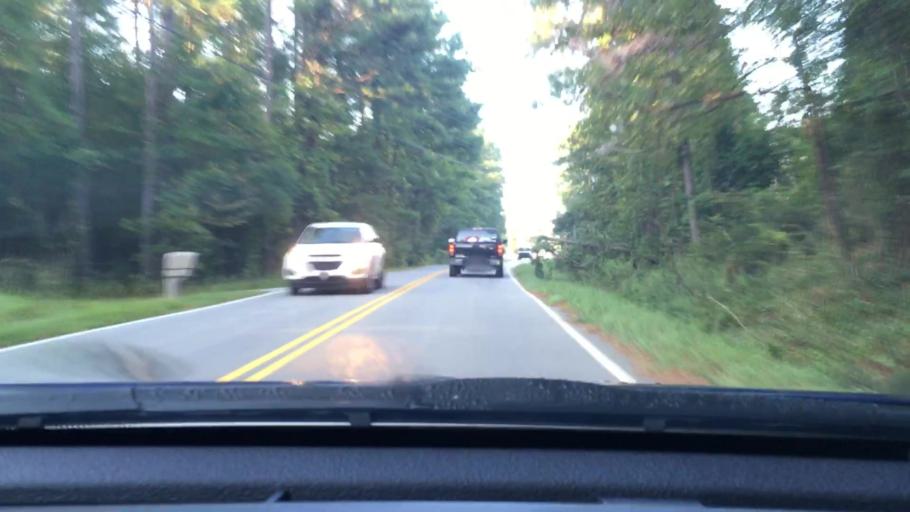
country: US
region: South Carolina
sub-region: Lexington County
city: Irmo
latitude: 34.0974
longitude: -81.1547
